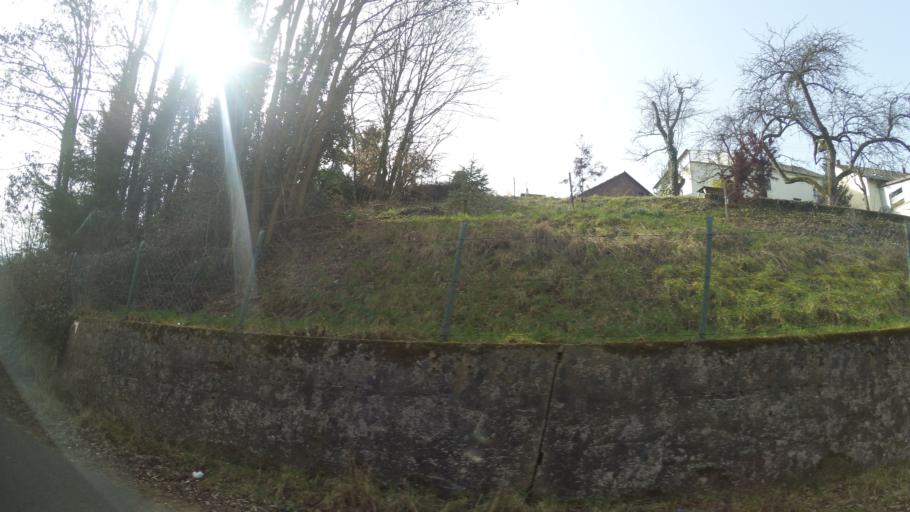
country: DE
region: Saarland
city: Schmelz
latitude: 49.4449
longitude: 6.8451
